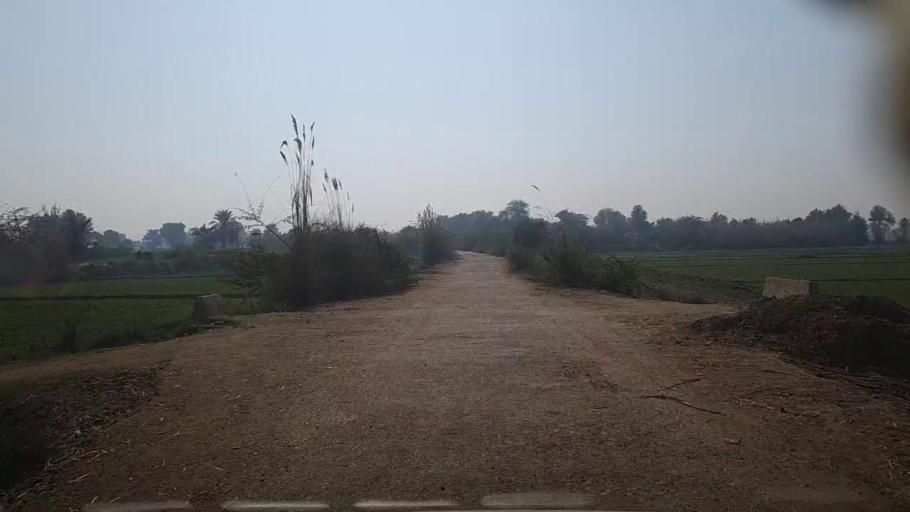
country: PK
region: Sindh
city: Kandiari
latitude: 26.9798
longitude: 68.4694
